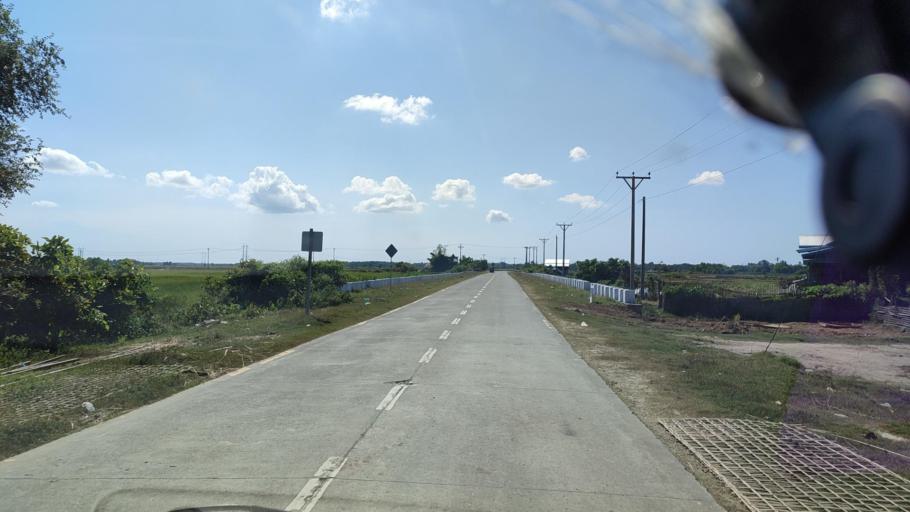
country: MM
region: Rakhine
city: Sittwe
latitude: 20.2939
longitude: 92.8813
